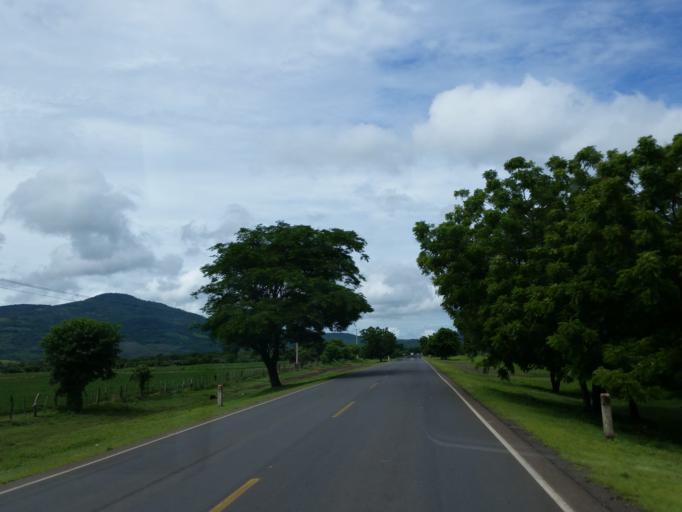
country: NI
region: Leon
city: Larreynaga
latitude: 12.5975
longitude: -86.7007
